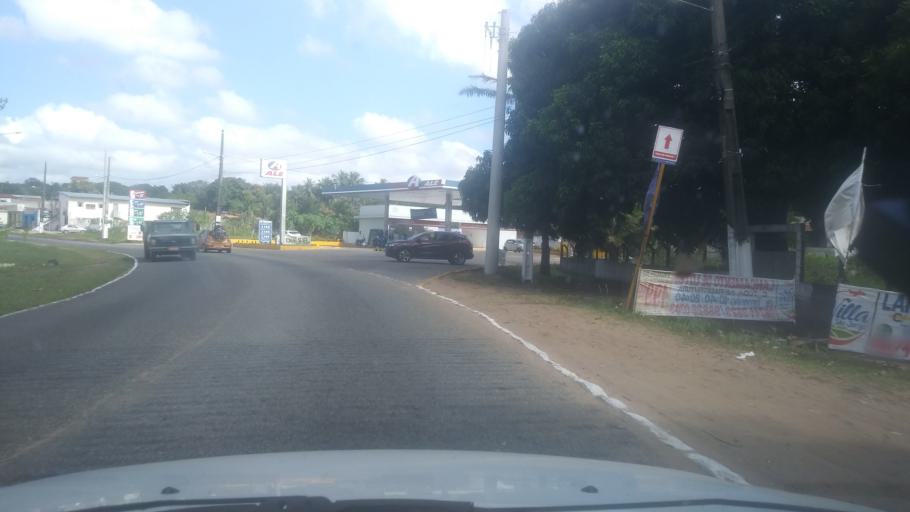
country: BR
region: Rio Grande do Norte
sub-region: Extremoz
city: Extremoz
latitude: -5.7042
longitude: -35.2820
